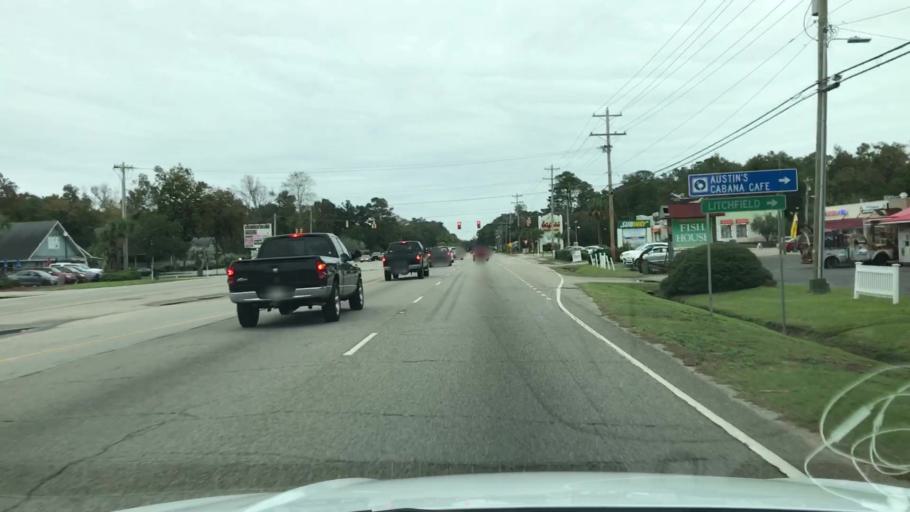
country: US
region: South Carolina
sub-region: Georgetown County
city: Murrells Inlet
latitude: 33.4706
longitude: -79.1055
